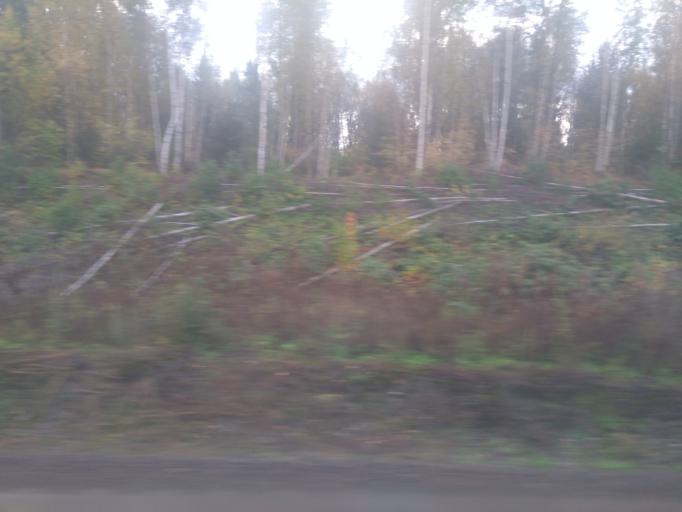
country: RU
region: Udmurtiya
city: Mozhga
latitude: 56.4264
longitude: 52.0503
